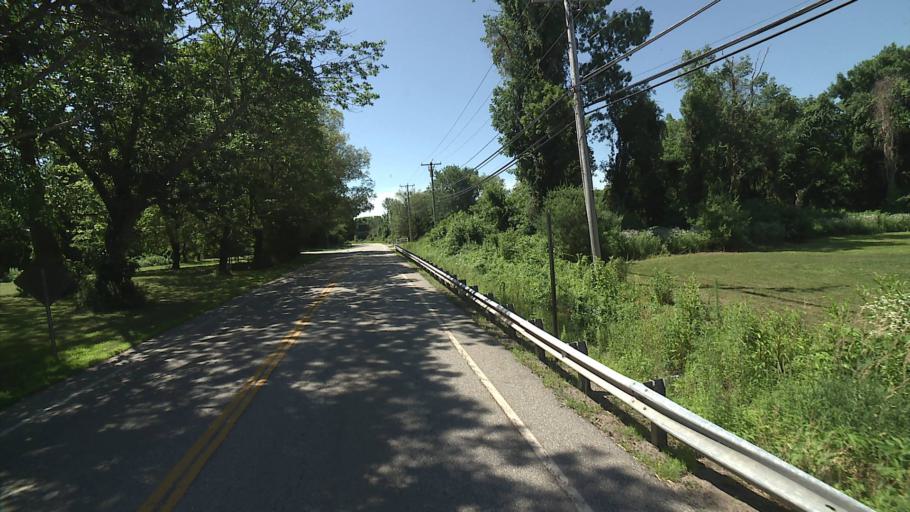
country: US
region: Connecticut
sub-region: Windham County
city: Willimantic
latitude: 41.6504
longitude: -72.2263
